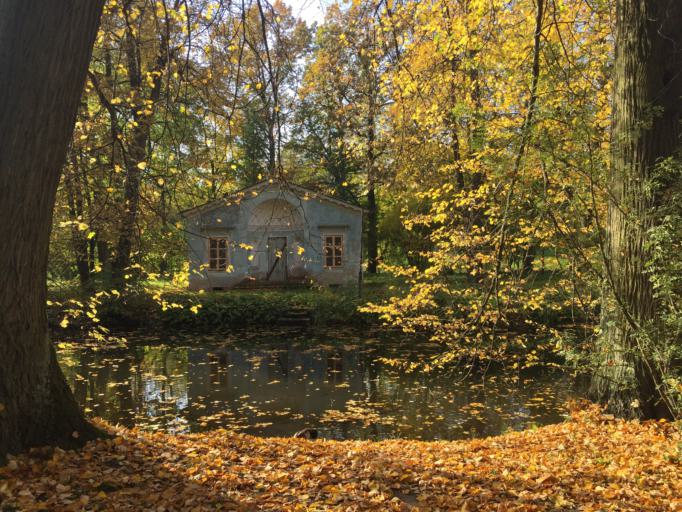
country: RU
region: St.-Petersburg
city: Pushkin
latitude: 59.7213
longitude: 30.3900
